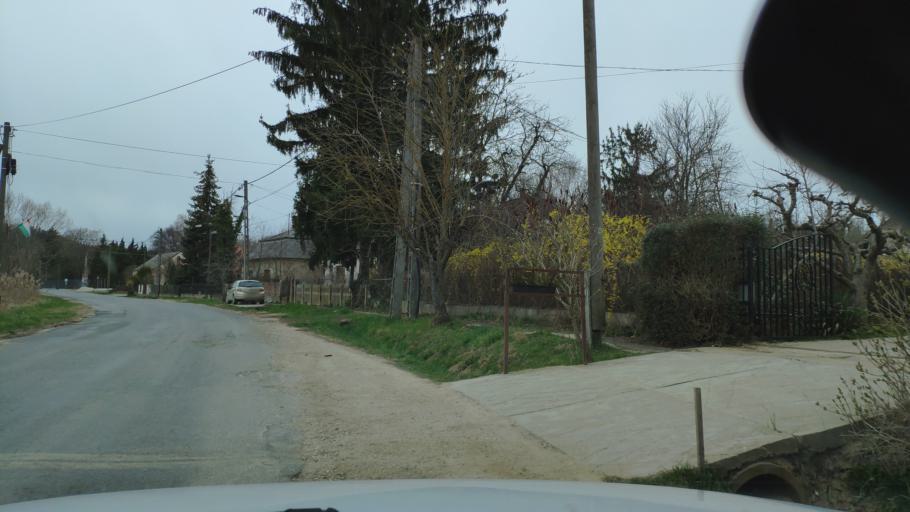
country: HU
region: Zala
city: Pacsa
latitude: 46.6748
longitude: 17.0649
